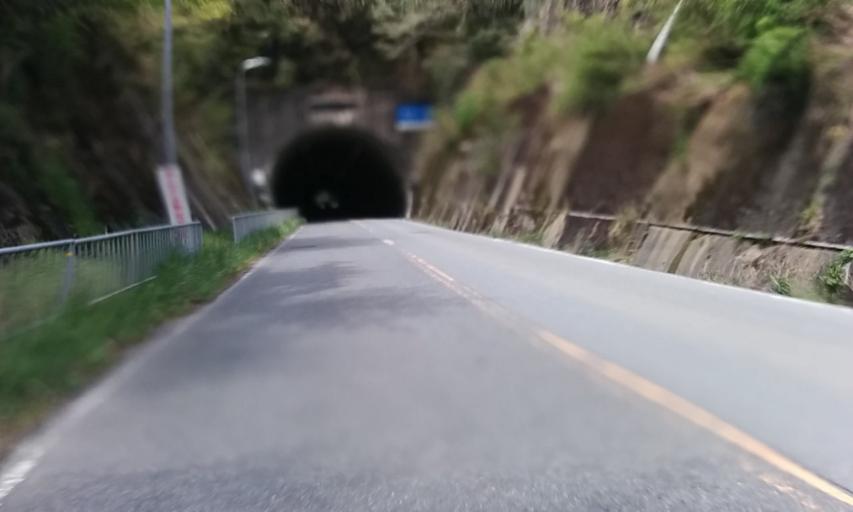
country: JP
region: Kyoto
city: Kameoka
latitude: 34.9637
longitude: 135.5895
